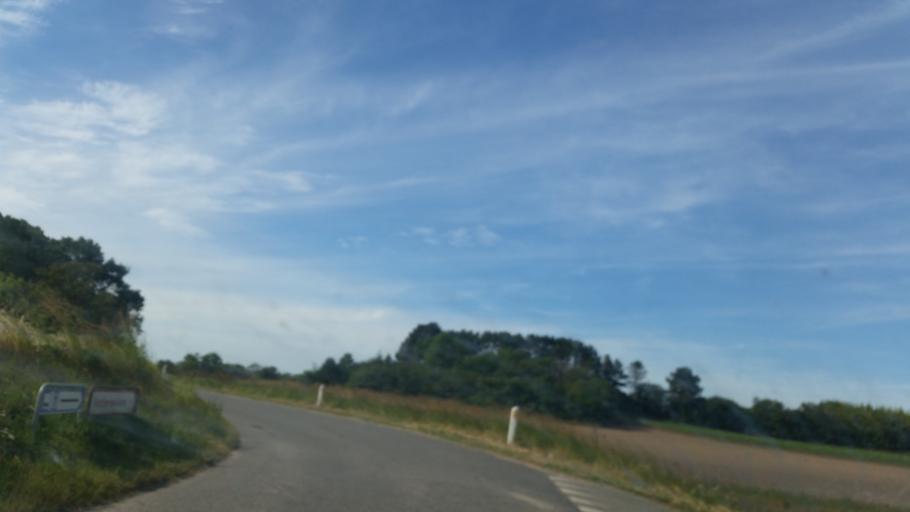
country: DK
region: Central Jutland
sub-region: Samso Kommune
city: Tranebjerg
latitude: 55.8224
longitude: 10.5388
